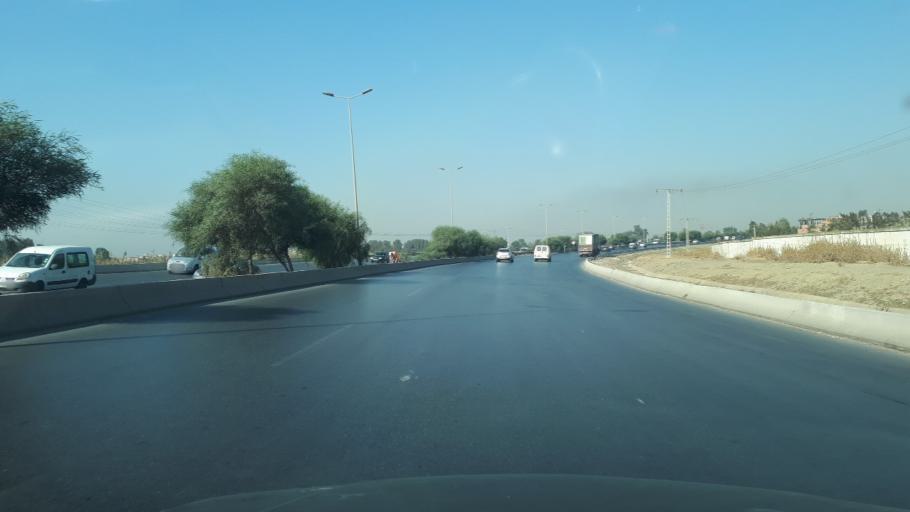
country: DZ
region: Tipaza
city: Baraki
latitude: 36.6824
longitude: 3.1083
